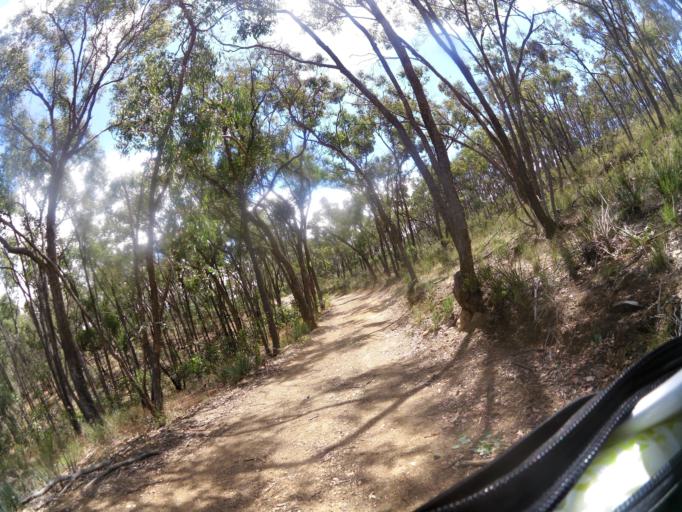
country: AU
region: Victoria
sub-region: Mount Alexander
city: Castlemaine
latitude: -37.0712
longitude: 144.2629
